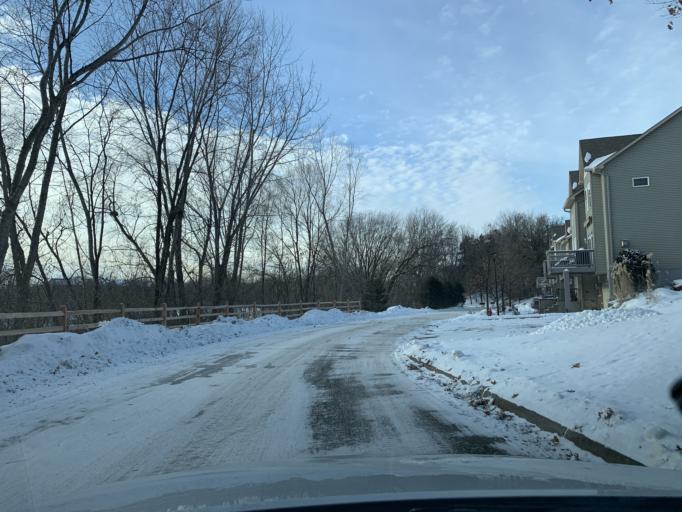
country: US
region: Minnesota
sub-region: Hennepin County
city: Minnetonka Mills
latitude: 44.9523
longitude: -93.4039
